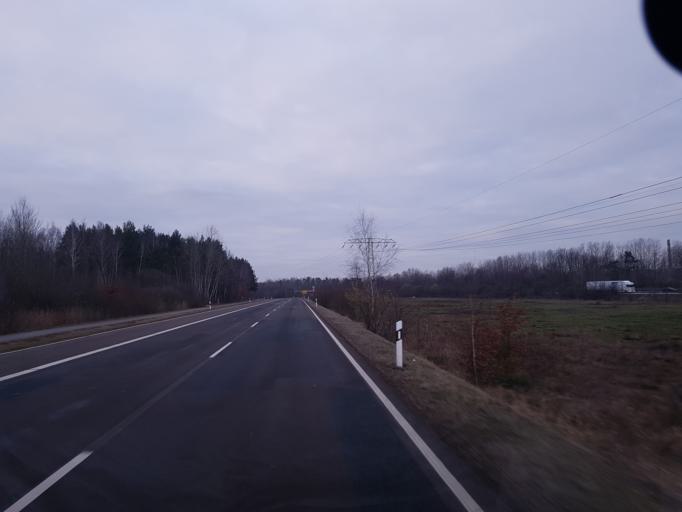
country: DE
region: Brandenburg
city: Schipkau
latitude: 51.5261
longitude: 13.9075
